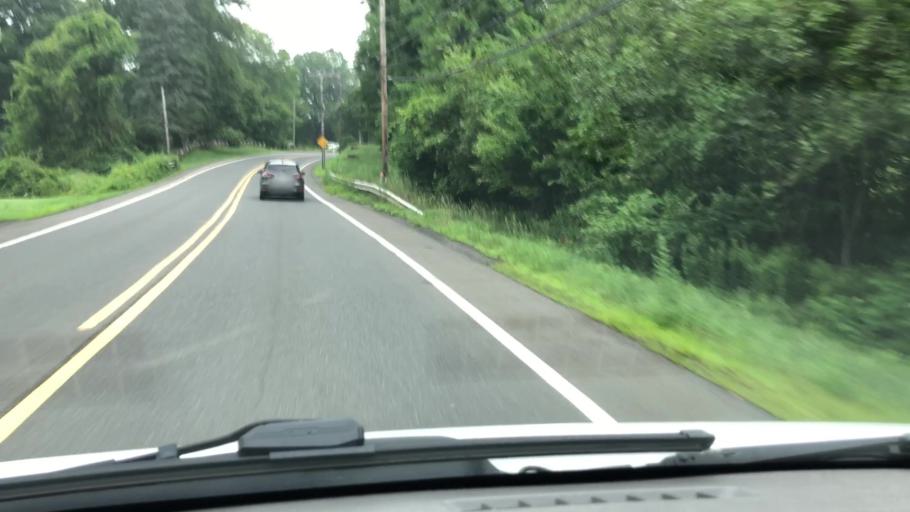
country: US
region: Massachusetts
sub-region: Franklin County
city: South Deerfield
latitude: 42.5234
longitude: -72.6072
